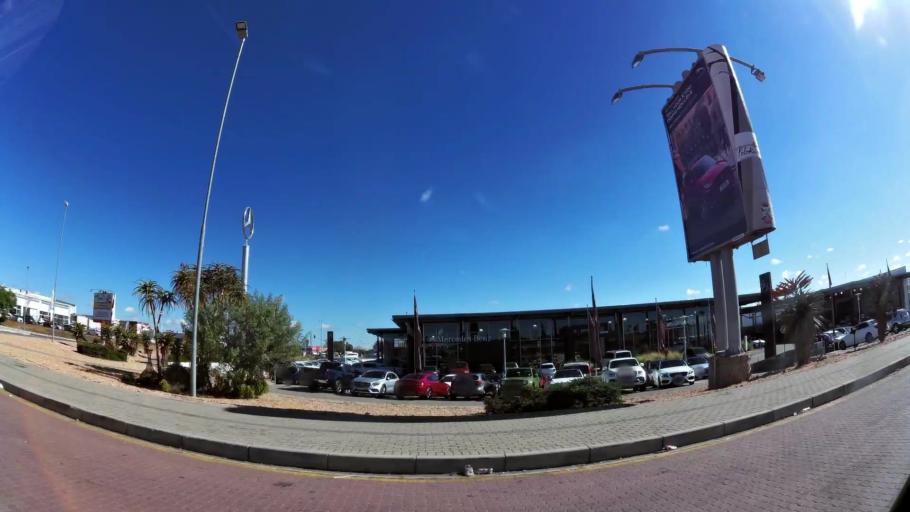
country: ZA
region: Limpopo
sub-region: Capricorn District Municipality
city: Polokwane
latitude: -23.9148
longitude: 29.4442
